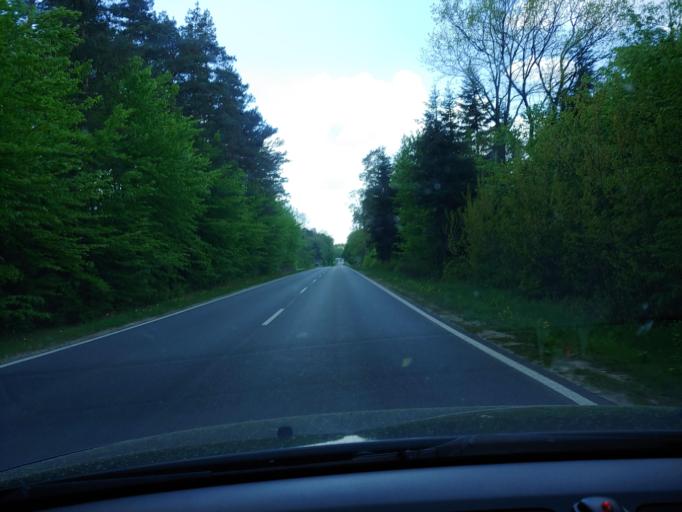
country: PL
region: Lesser Poland Voivodeship
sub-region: Powiat tarnowski
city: Jodlowka-Walki
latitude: 50.1320
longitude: 21.1562
